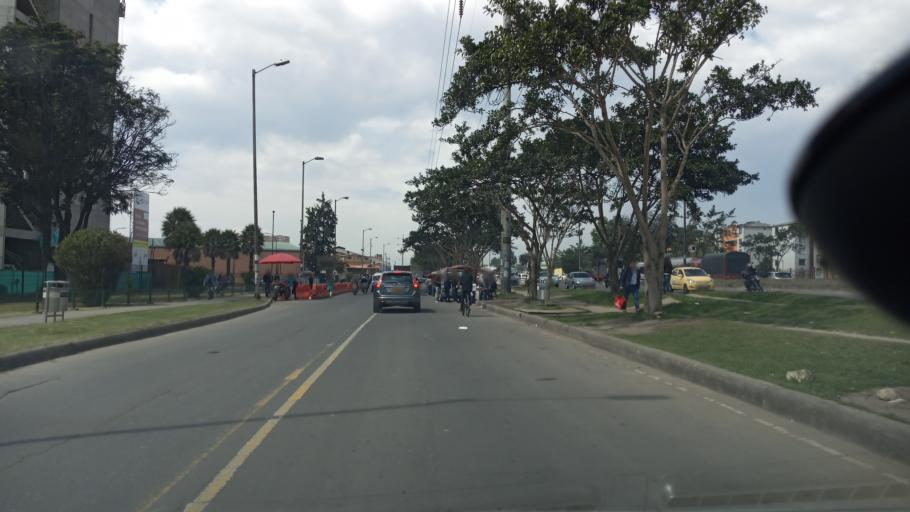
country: CO
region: Cundinamarca
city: Funza
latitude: 4.6753
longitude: -74.1535
